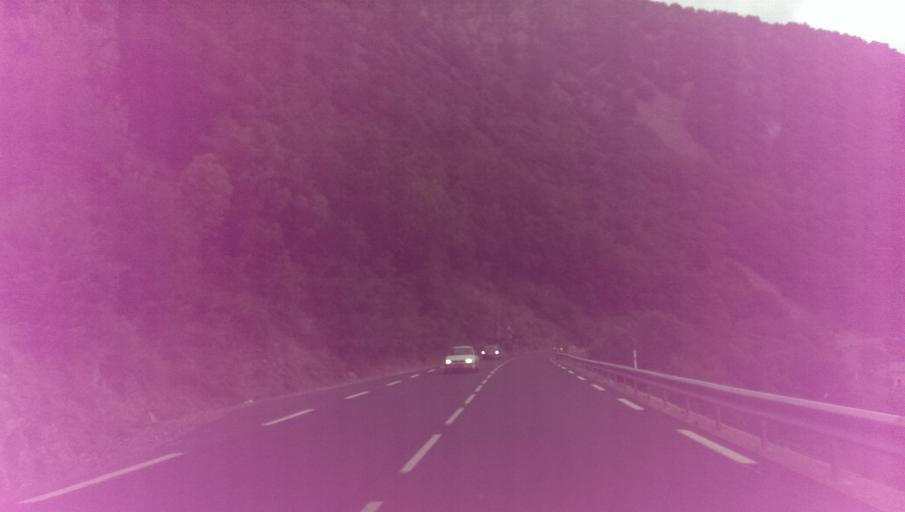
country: ES
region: Catalonia
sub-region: Provincia de Girona
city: Llivia
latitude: 42.5097
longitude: 2.1759
